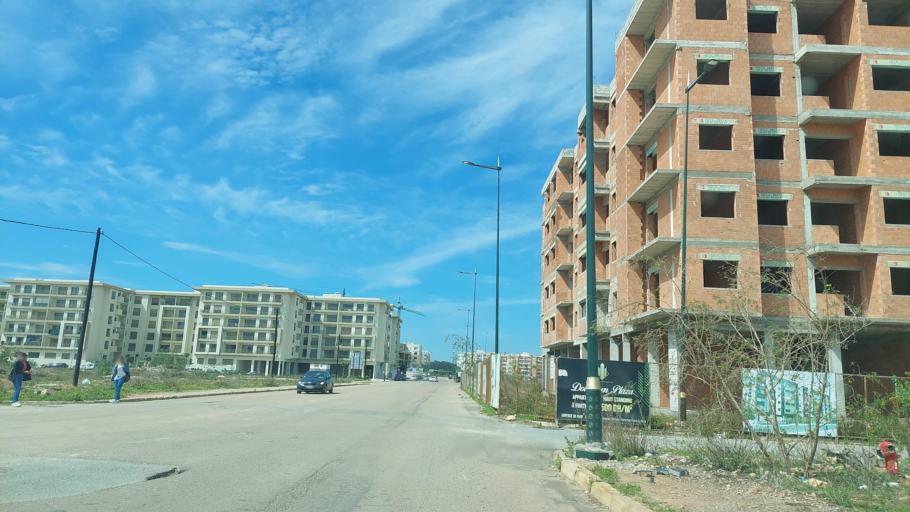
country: MA
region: Chaouia-Ouardigha
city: Nouaseur
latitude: 33.3935
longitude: -7.5574
